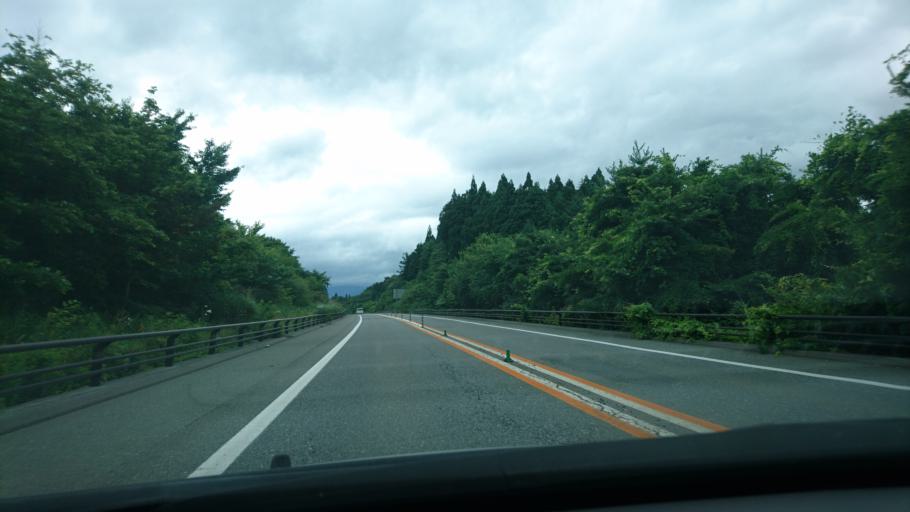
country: JP
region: Iwate
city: Ofunato
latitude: 39.0438
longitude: 141.7155
